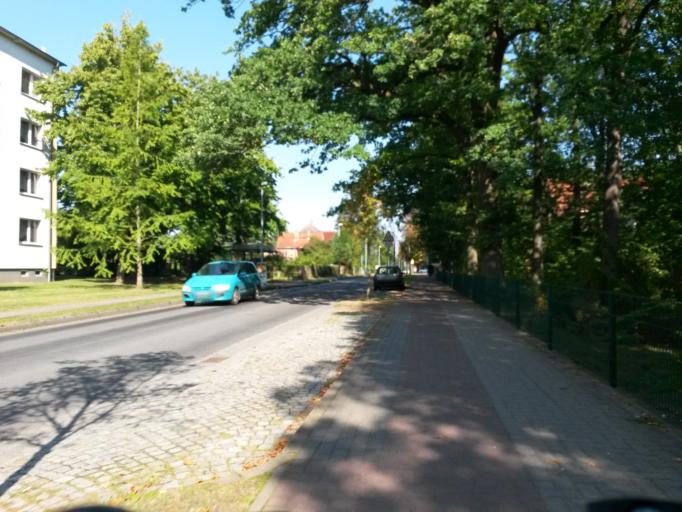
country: DE
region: Brandenburg
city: Templin
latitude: 53.1194
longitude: 13.4838
